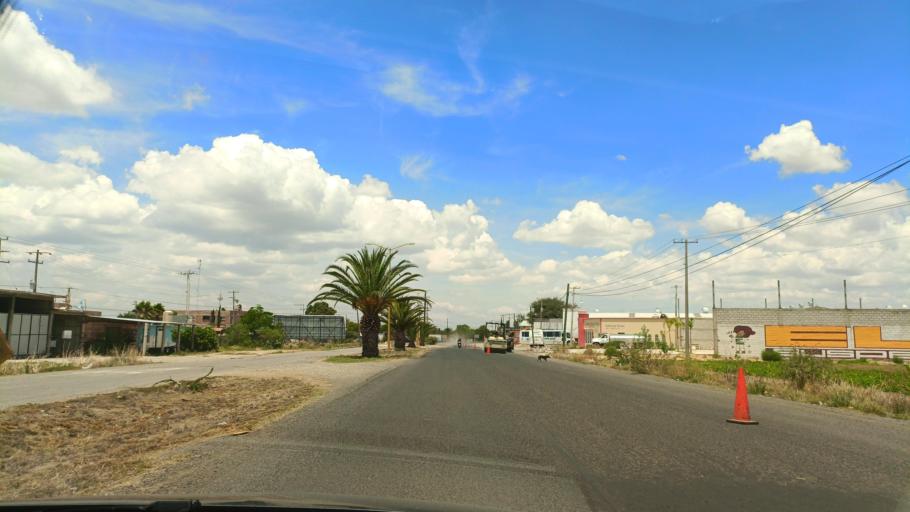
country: MX
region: Guanajuato
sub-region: San Luis de la Paz
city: San Ignacio
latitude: 21.2883
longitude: -100.5548
